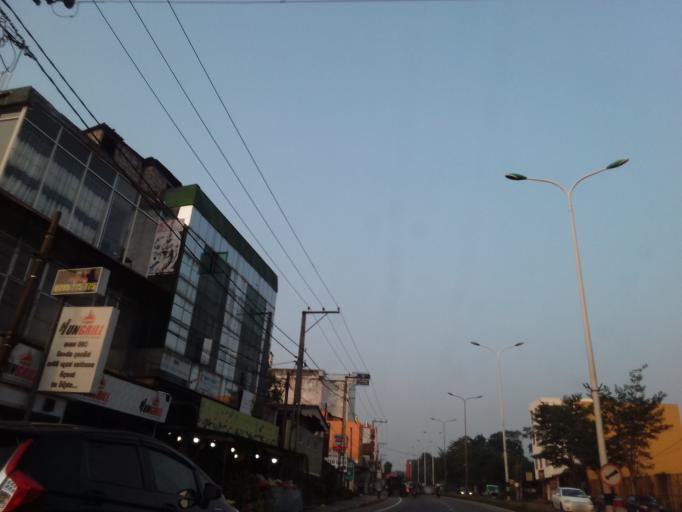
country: LK
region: Western
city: Kelaniya
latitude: 6.9877
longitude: 79.9370
